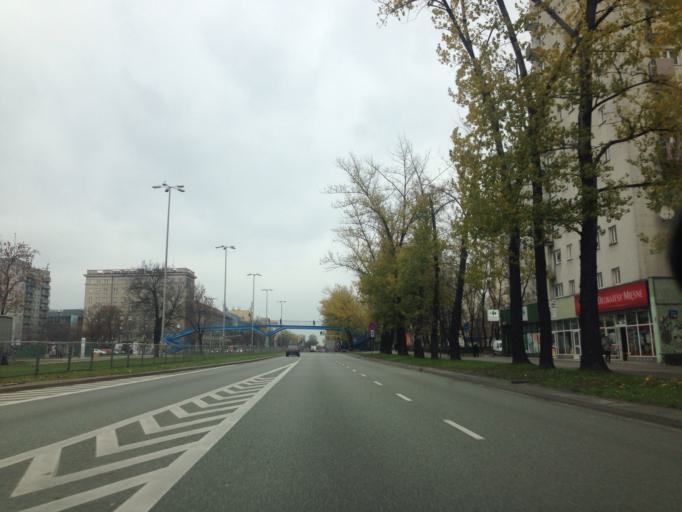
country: PL
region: Masovian Voivodeship
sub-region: Warszawa
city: Mokotow
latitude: 52.2005
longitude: 21.0506
